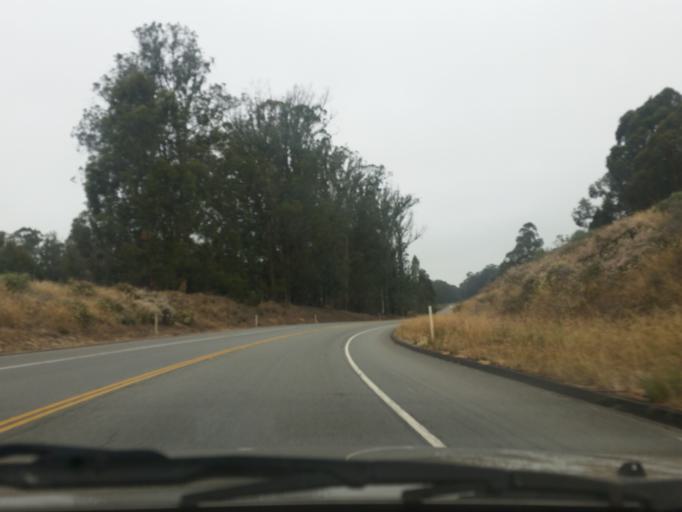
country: US
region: California
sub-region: San Luis Obispo County
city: Callender
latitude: 35.0528
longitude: -120.5953
